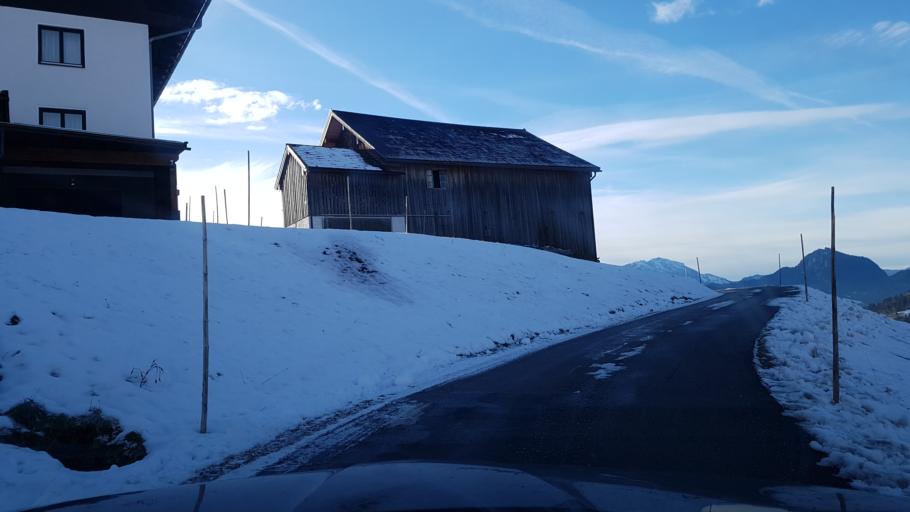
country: AT
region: Salzburg
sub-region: Politischer Bezirk Hallein
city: Abtenau
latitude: 47.5723
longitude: 13.4095
